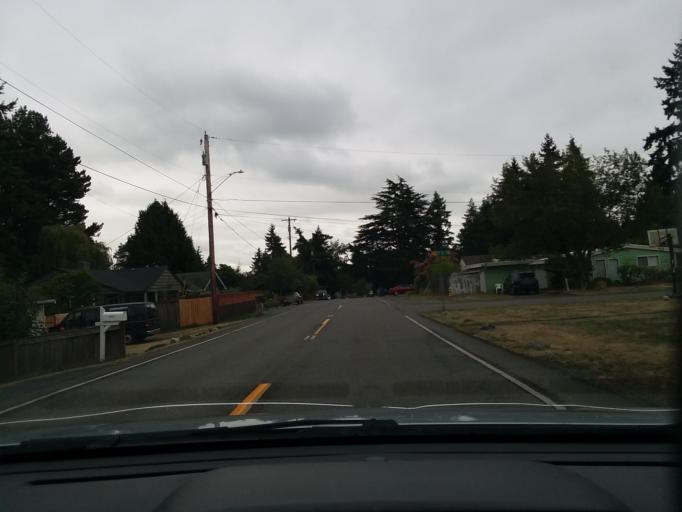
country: US
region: Washington
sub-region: Snohomish County
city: Esperance
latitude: 47.7954
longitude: -122.3322
